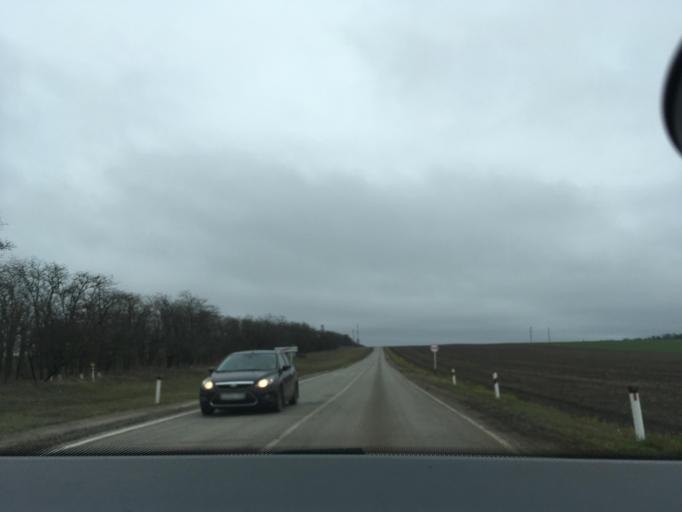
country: RU
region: Krasnodarskiy
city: Kushchevskaya
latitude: 46.5870
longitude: 39.6426
